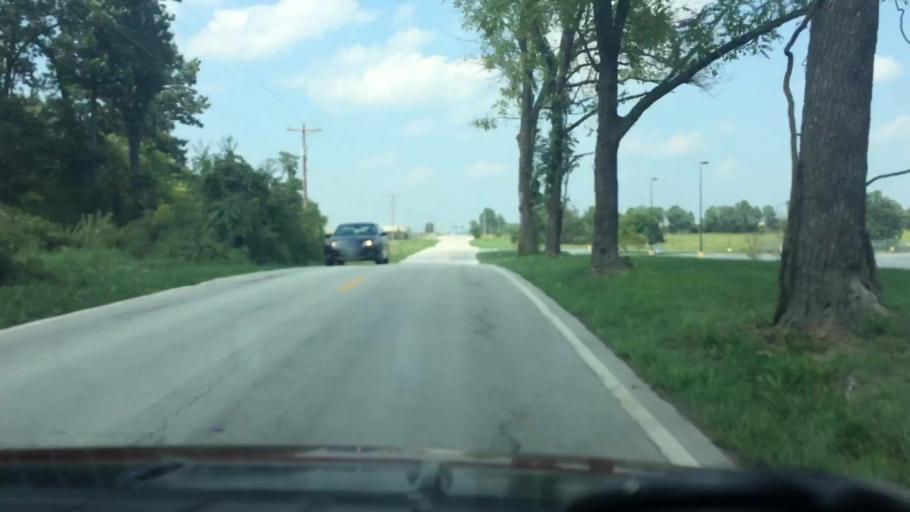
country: US
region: Missouri
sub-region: Greene County
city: Strafford
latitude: 37.2428
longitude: -93.1835
